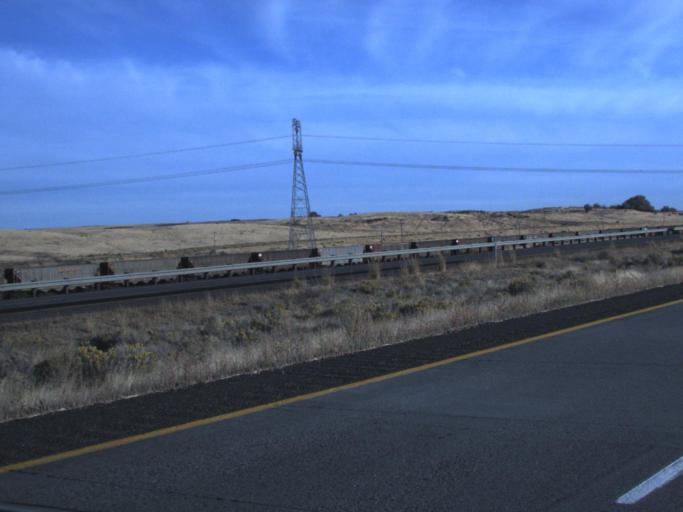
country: US
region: Washington
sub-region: Franklin County
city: Basin City
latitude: 46.5410
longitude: -119.0103
